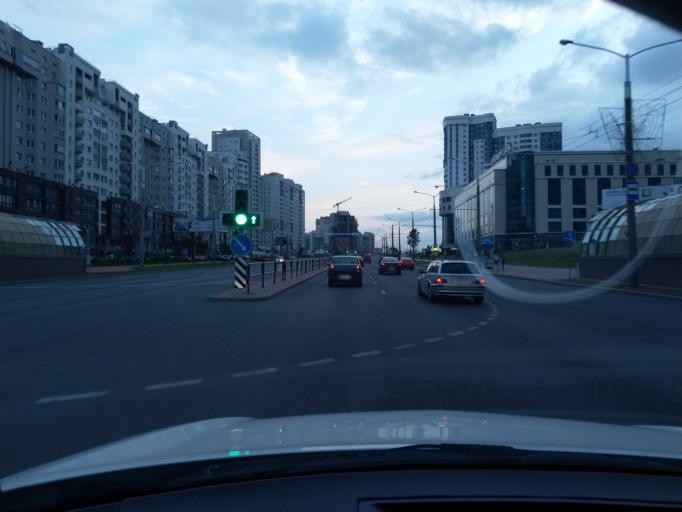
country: BY
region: Minsk
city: Minsk
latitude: 53.8910
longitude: 27.5246
